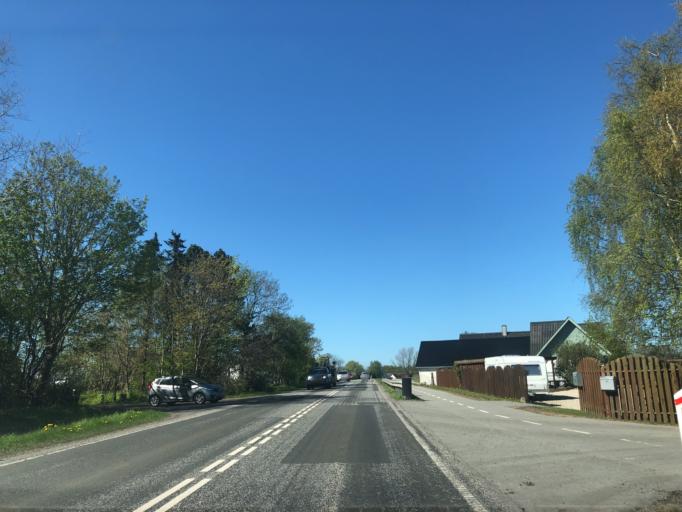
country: DK
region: Zealand
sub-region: Stevns Kommune
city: Harlev
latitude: 55.3688
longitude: 12.3018
